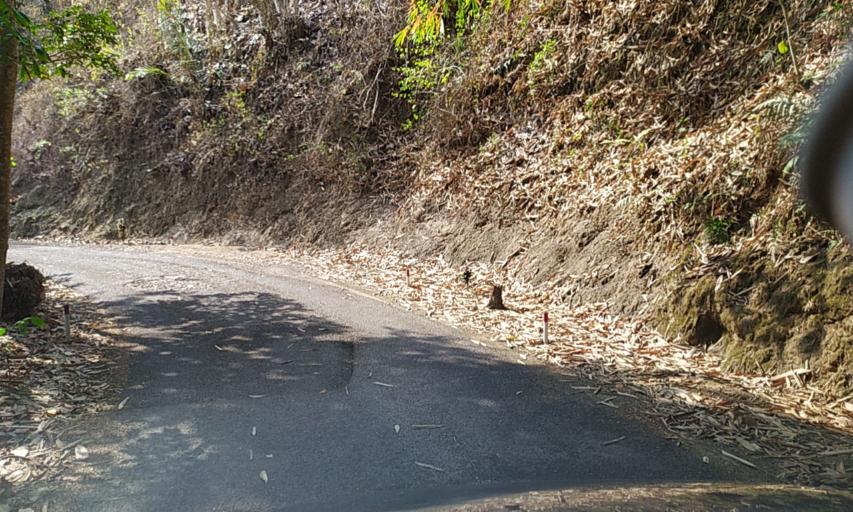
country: ID
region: Central Java
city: Pasirmanggu
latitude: -7.2336
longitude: 108.5903
